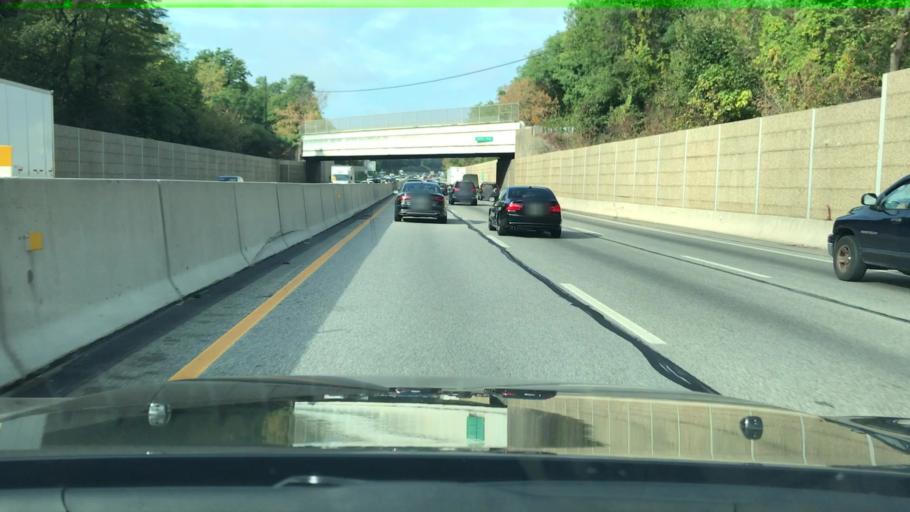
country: US
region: Pennsylvania
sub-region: Montgomery County
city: Fort Washington
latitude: 40.1250
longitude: -75.2284
